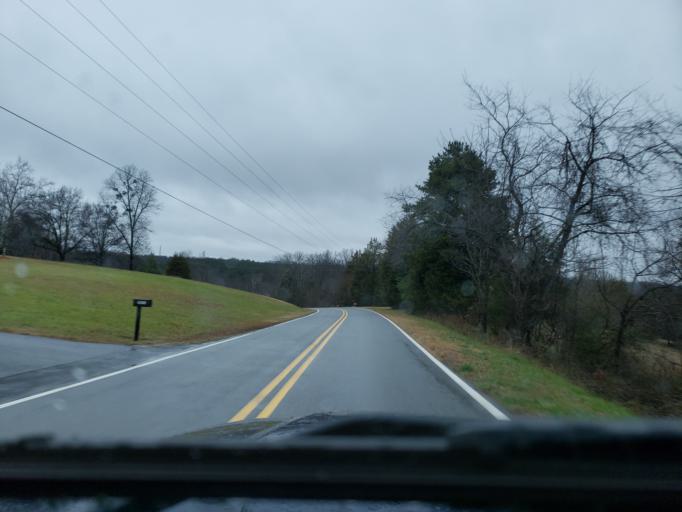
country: US
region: North Carolina
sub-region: Cleveland County
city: White Plains
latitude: 35.1799
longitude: -81.3703
